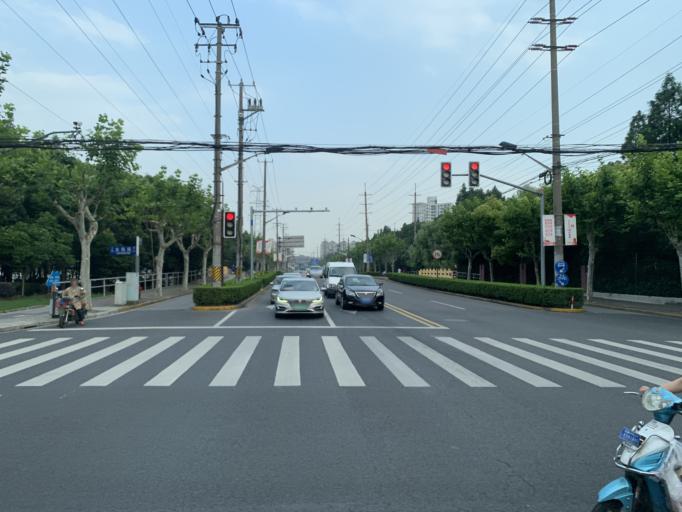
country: CN
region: Shanghai Shi
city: Pudong
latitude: 31.2481
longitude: 121.5664
